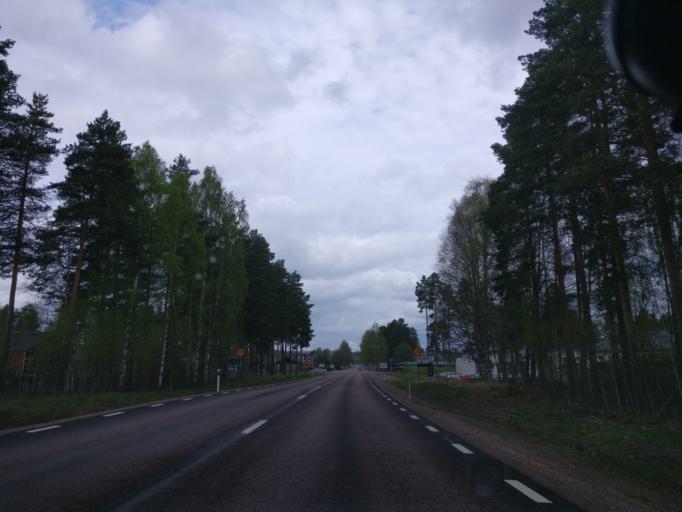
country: SE
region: Vaermland
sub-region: Hagfors Kommun
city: Ekshaerad
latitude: 60.1677
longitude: 13.4981
